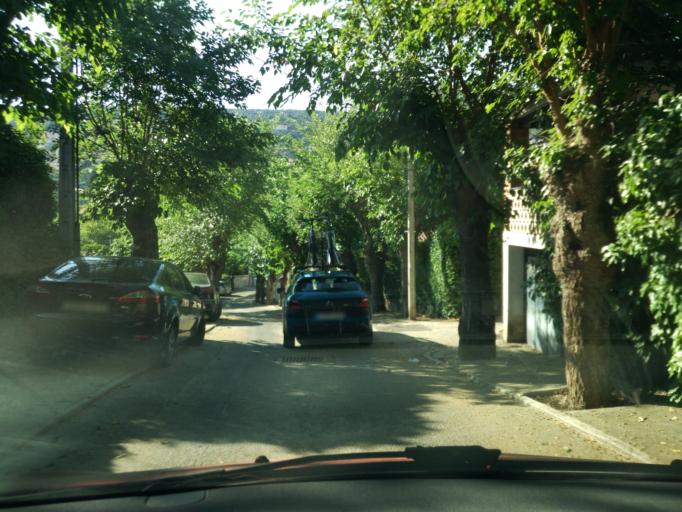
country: ES
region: Madrid
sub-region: Provincia de Madrid
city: Ambite
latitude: 40.3278
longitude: -3.1804
